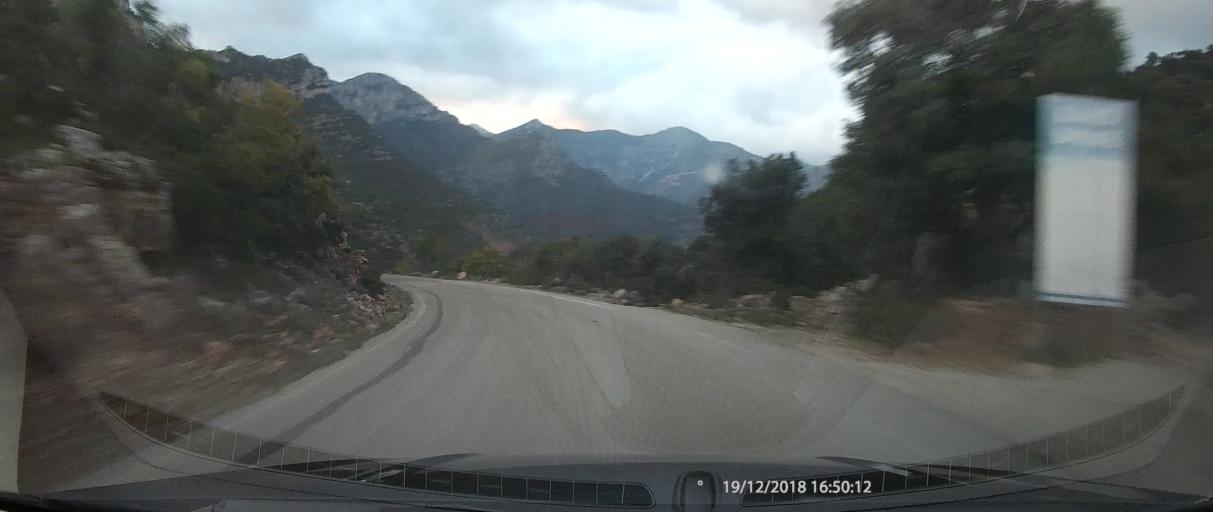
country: GR
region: Peloponnese
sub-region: Nomos Lakonias
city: Sykea
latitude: 36.9513
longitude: 22.9959
